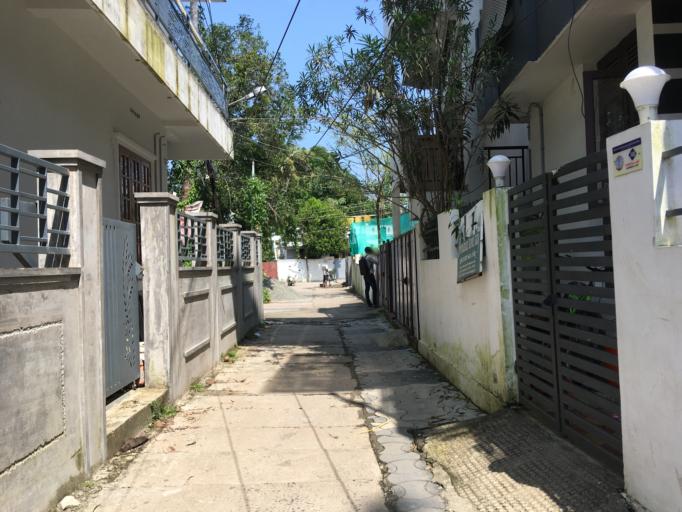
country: IN
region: Kerala
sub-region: Ernakulam
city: Cochin
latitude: 9.9601
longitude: 76.2442
